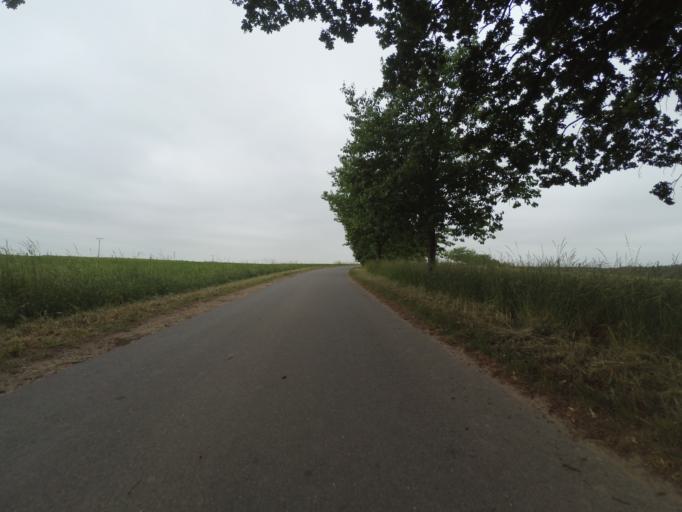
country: DE
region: Mecklenburg-Vorpommern
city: Goldberg
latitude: 53.5553
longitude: 12.0269
